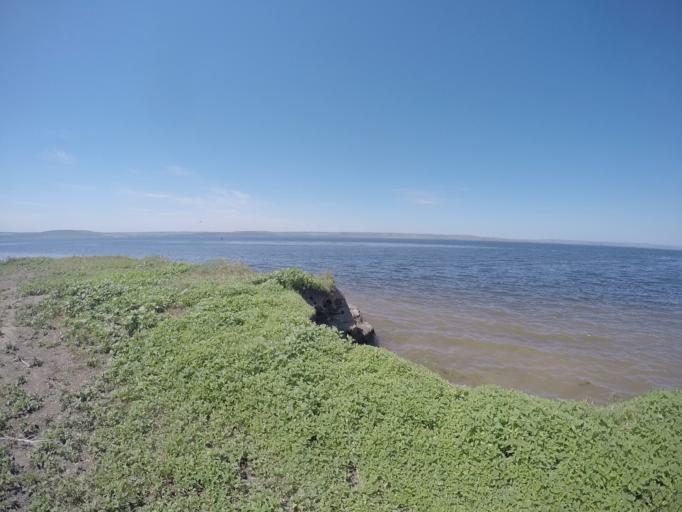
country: RU
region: Saratov
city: Krasnoarmeysk
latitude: 51.1564
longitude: 45.8981
